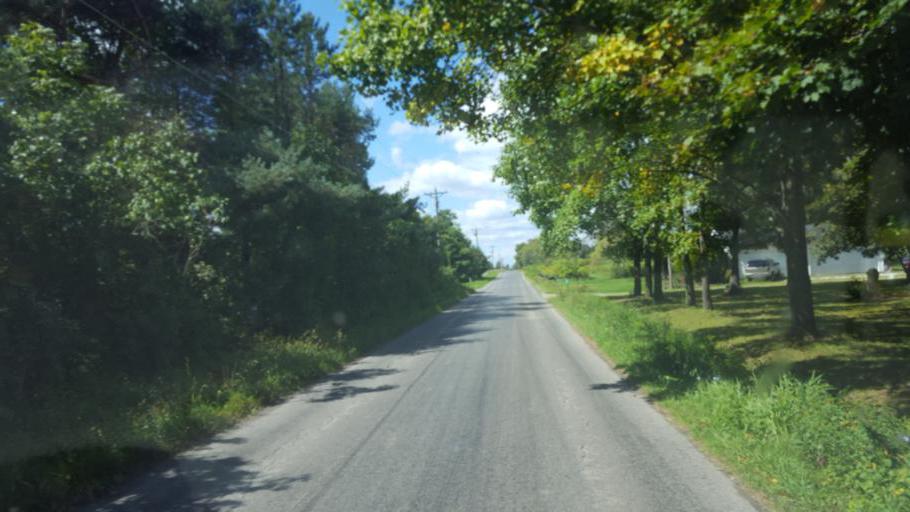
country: US
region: Ohio
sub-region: Wayne County
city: West Salem
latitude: 41.0134
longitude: -82.2159
